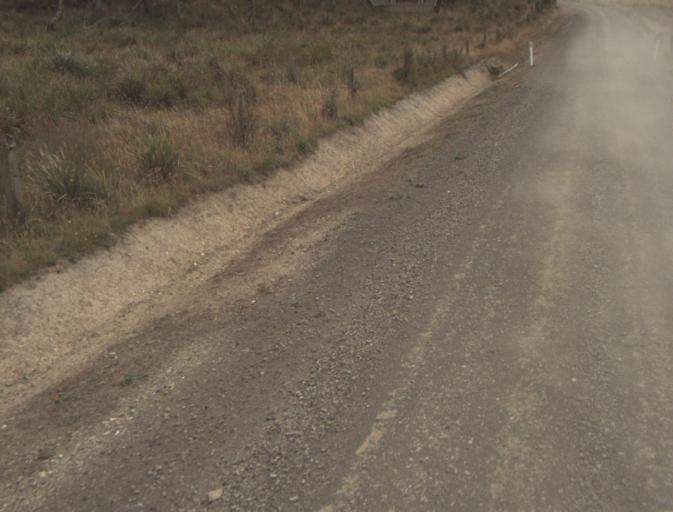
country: AU
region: Tasmania
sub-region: Northern Midlands
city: Evandale
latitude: -41.4740
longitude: 147.4458
